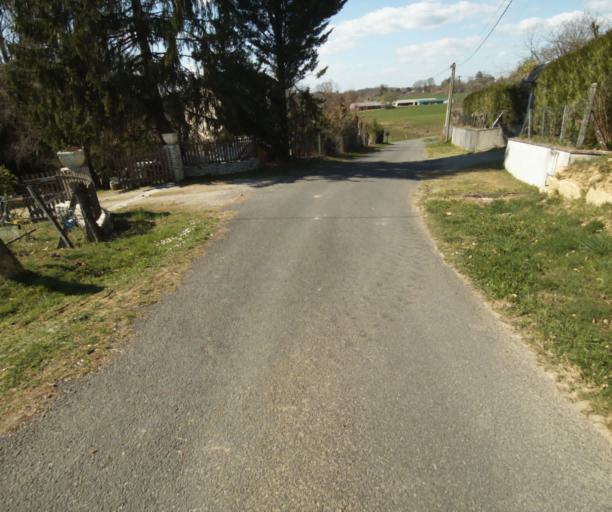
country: FR
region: Limousin
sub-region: Departement de la Correze
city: Saint-Mexant
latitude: 45.2912
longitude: 1.6729
